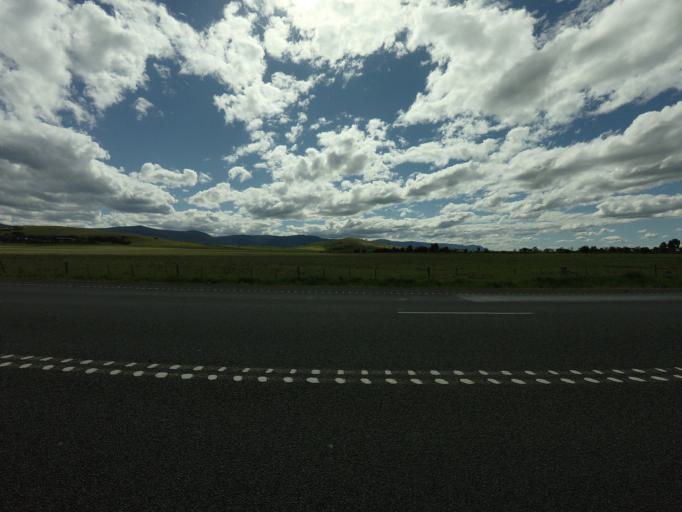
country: AU
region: Tasmania
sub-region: Brighton
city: Bridgewater
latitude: -42.1693
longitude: 147.3949
